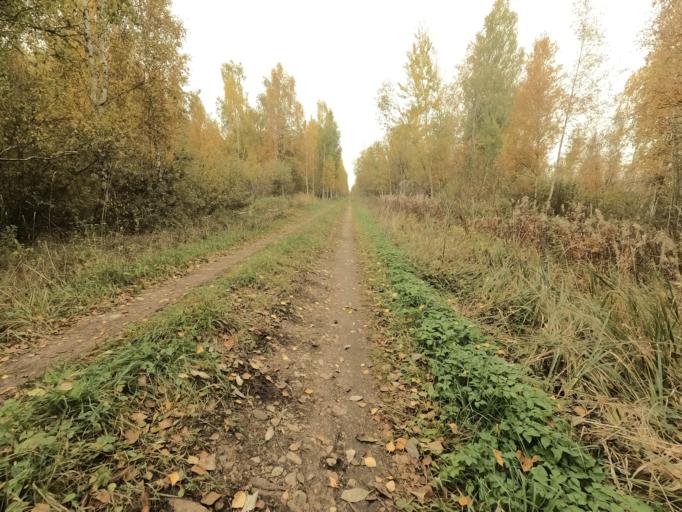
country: RU
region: Novgorod
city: Pankovka
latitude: 58.8862
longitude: 30.9468
